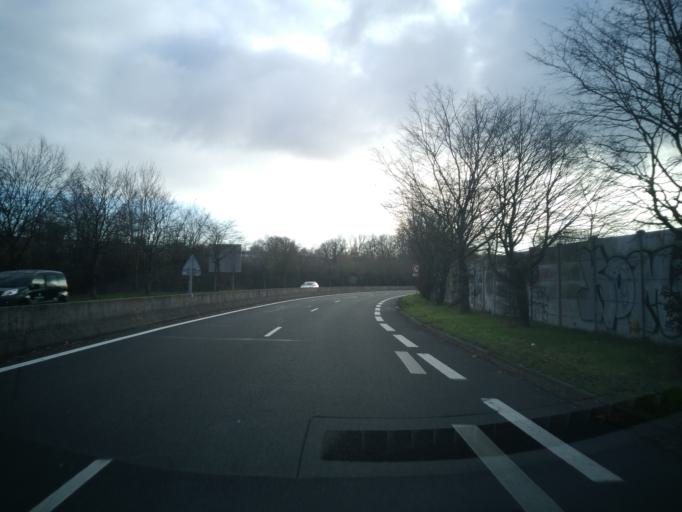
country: FR
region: Ile-de-France
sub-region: Departement des Yvelines
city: Buc
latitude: 48.7834
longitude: 2.1063
